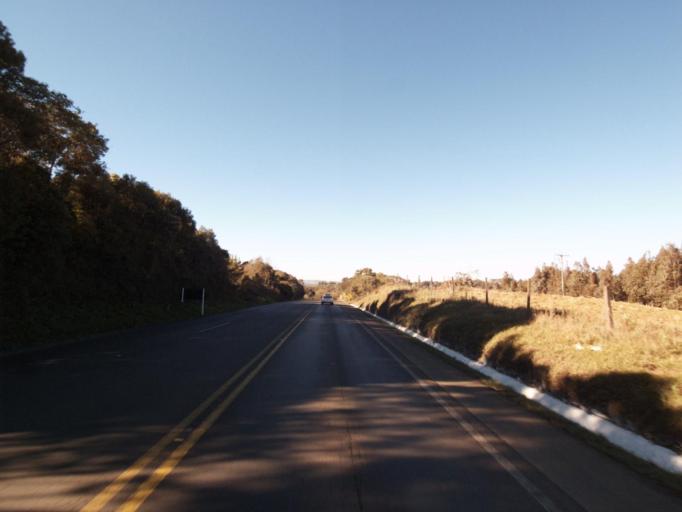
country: BR
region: Santa Catarina
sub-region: Concordia
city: Concordia
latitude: -26.8953
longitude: -51.9789
